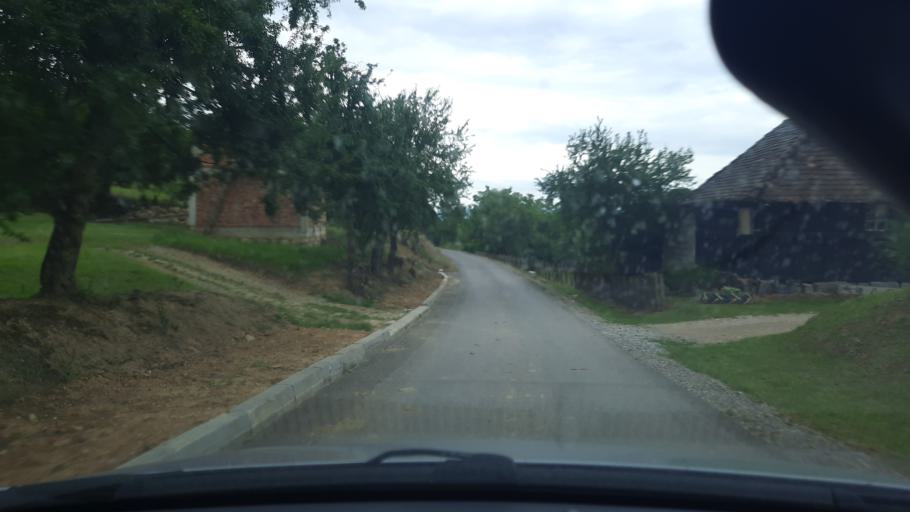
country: RS
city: Jarebice
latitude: 44.4987
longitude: 19.4761
